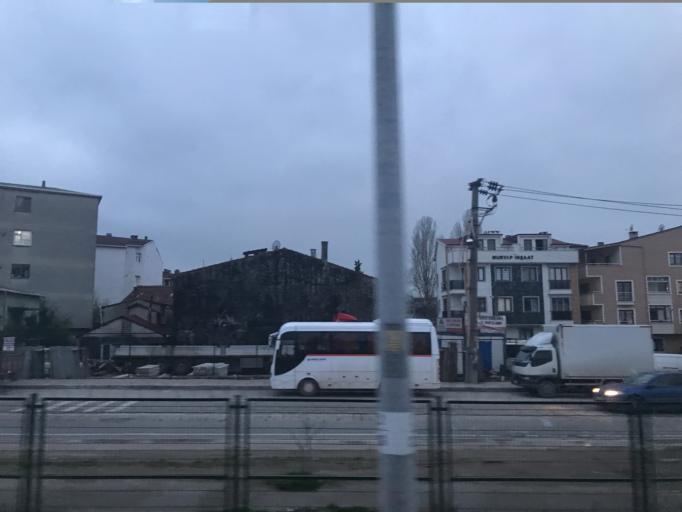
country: TR
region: Kocaeli
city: Darica
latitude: 40.7862
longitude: 29.4031
